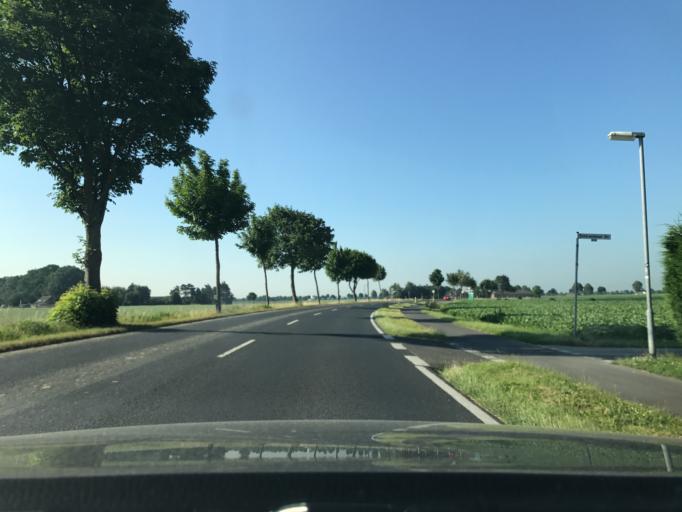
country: DE
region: North Rhine-Westphalia
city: Tonisvorst
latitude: 51.3473
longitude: 6.4652
